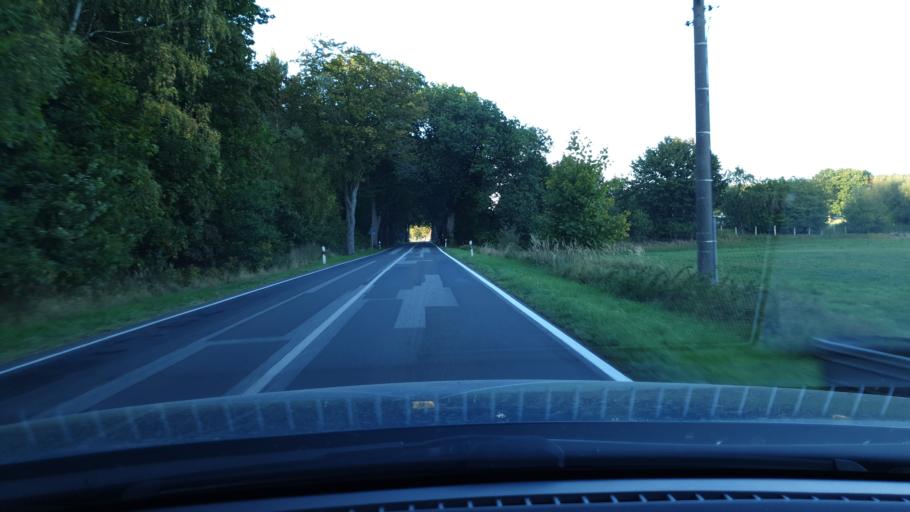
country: DE
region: Mecklenburg-Vorpommern
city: Wittenburg
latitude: 53.5661
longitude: 11.0982
